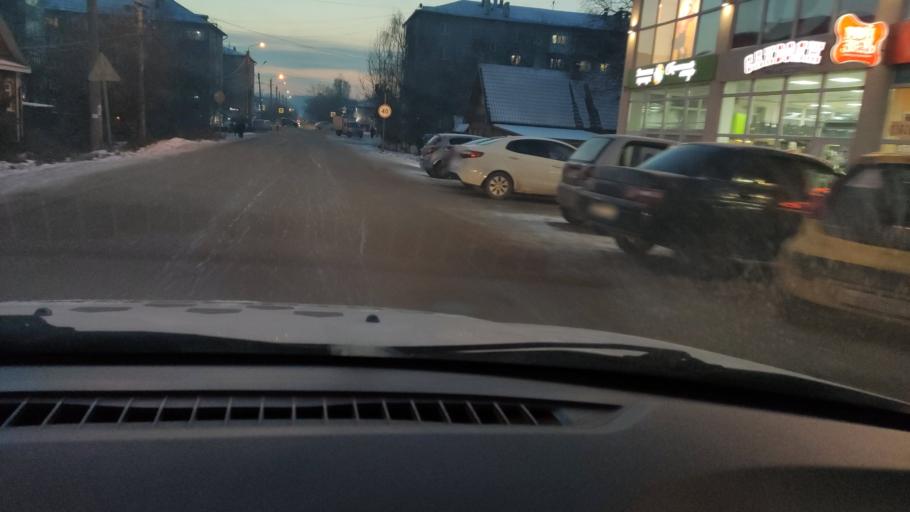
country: RU
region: Perm
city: Kungur
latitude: 57.4376
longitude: 56.9356
